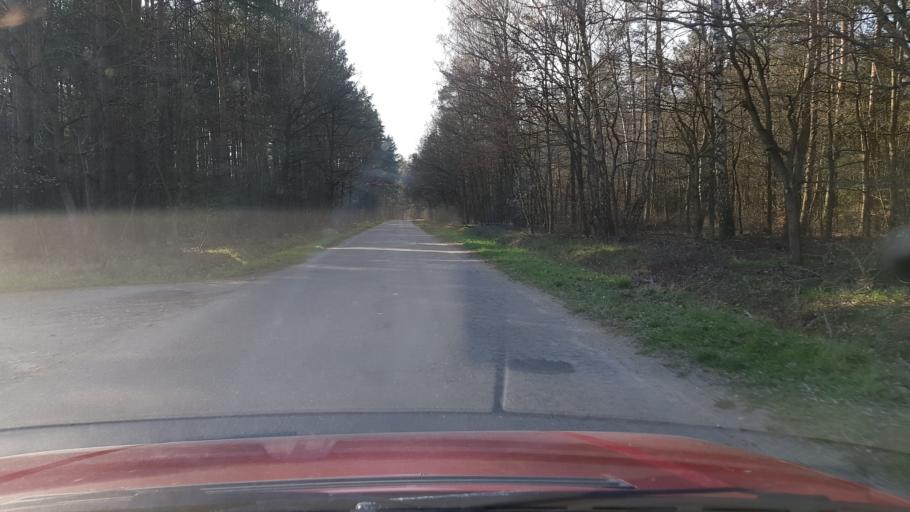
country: PL
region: West Pomeranian Voivodeship
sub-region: Powiat gryficki
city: Ploty
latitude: 53.8304
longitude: 15.3231
